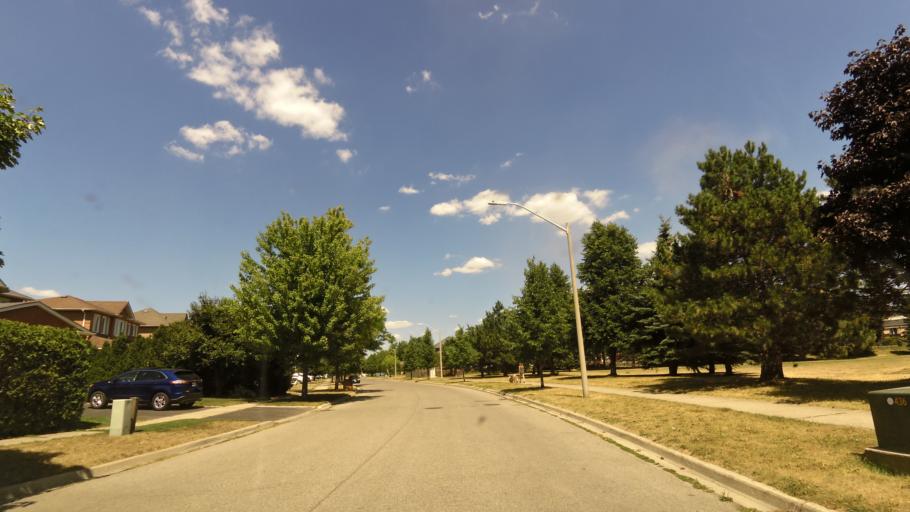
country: CA
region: Ontario
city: Brampton
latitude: 43.6398
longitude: -79.8717
